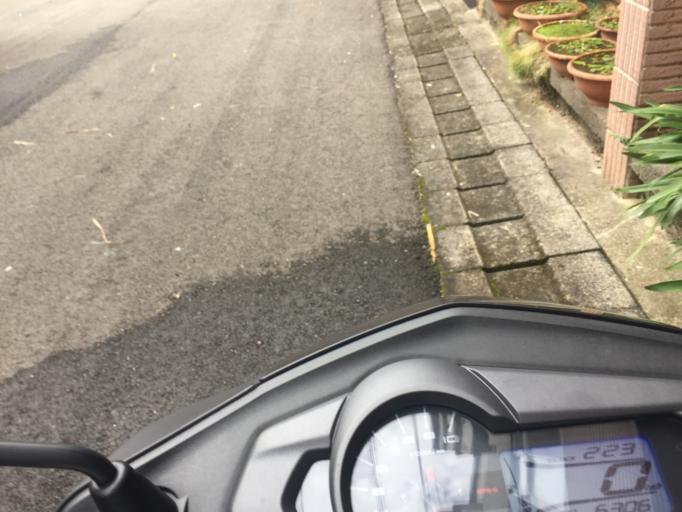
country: TW
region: Taiwan
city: Daxi
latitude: 24.7983
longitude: 121.1745
